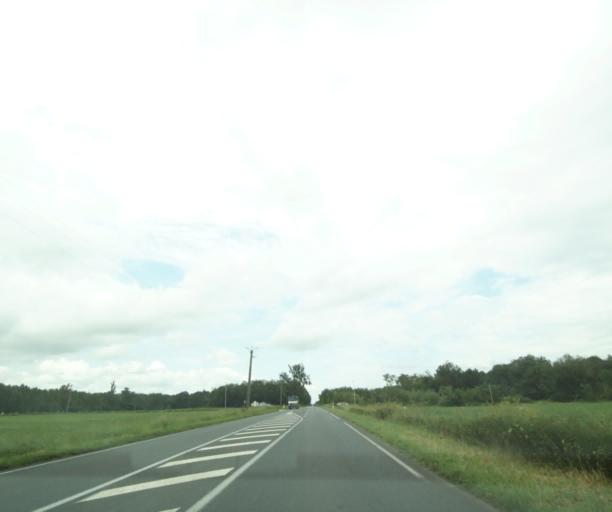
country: FR
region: Pays de la Loire
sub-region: Departement de Maine-et-Loire
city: Montreuil-Bellay
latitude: 47.0844
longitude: -0.1738
